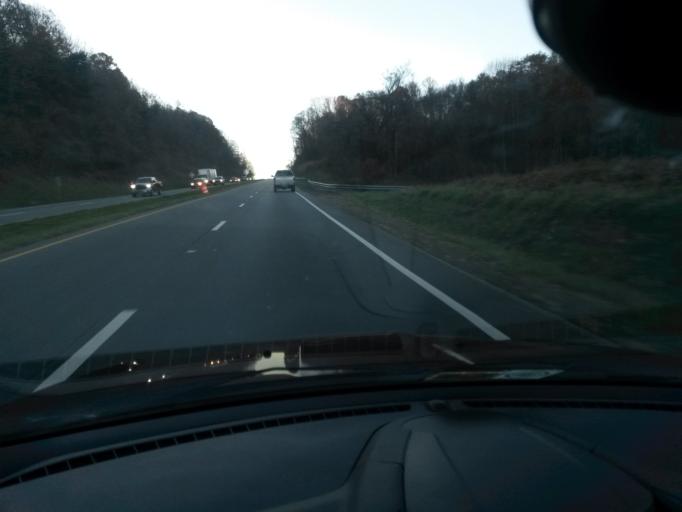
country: US
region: Virginia
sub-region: Roanoke County
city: Narrows
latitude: 37.1015
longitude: -79.9416
